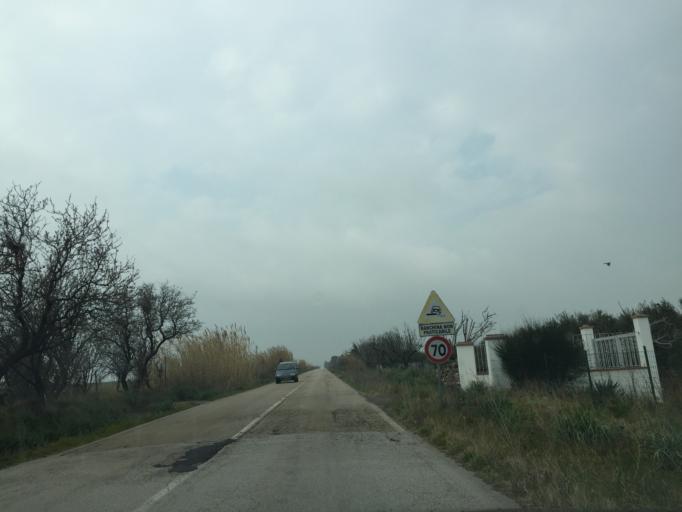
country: IT
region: Apulia
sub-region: Provincia di Foggia
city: Troia
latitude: 41.3935
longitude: 15.4125
